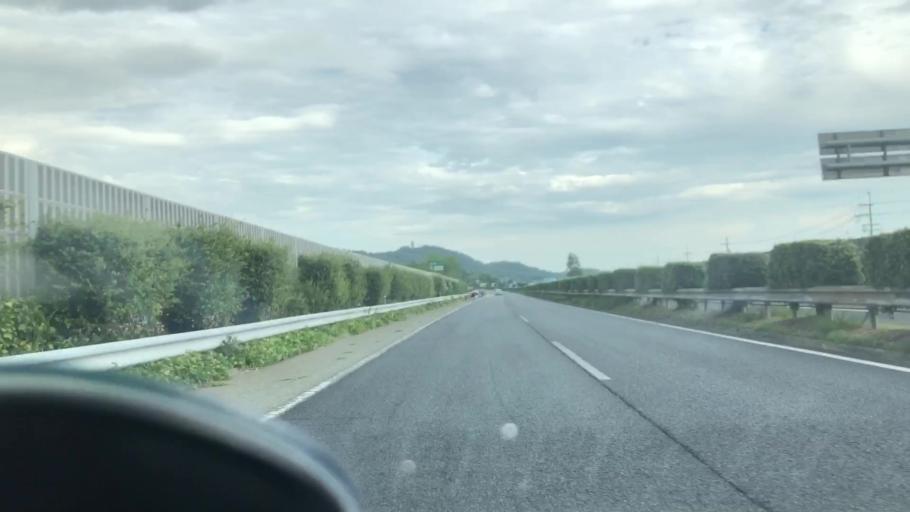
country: JP
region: Hyogo
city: Ono
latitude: 34.9372
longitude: 134.8330
